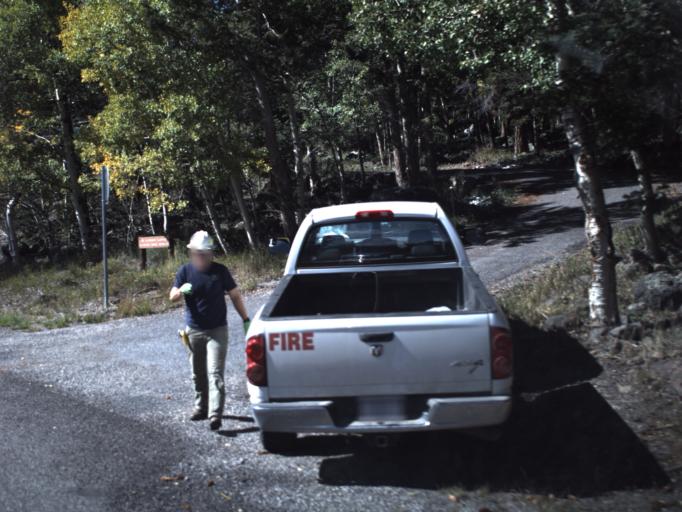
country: US
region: Utah
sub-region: Wayne County
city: Loa
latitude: 38.5425
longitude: -111.7314
